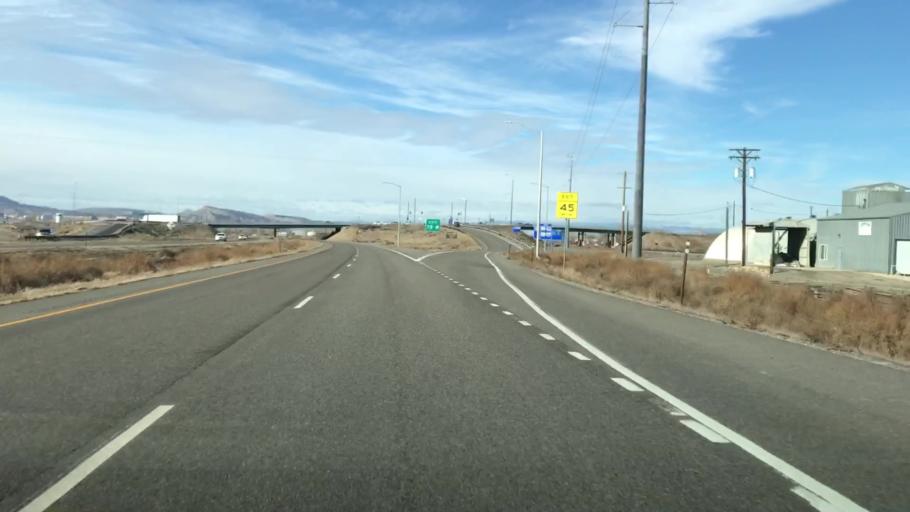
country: US
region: Colorado
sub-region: Mesa County
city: Fruita
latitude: 39.1530
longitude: -108.7326
